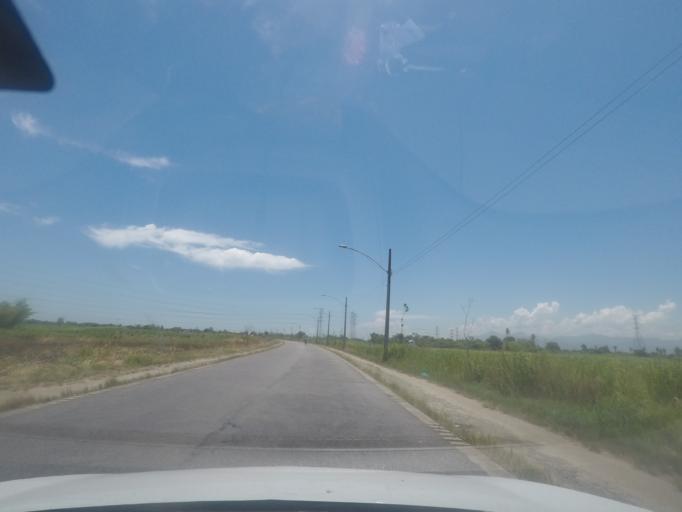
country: BR
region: Rio de Janeiro
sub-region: Itaguai
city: Itaguai
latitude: -22.8967
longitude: -43.6857
